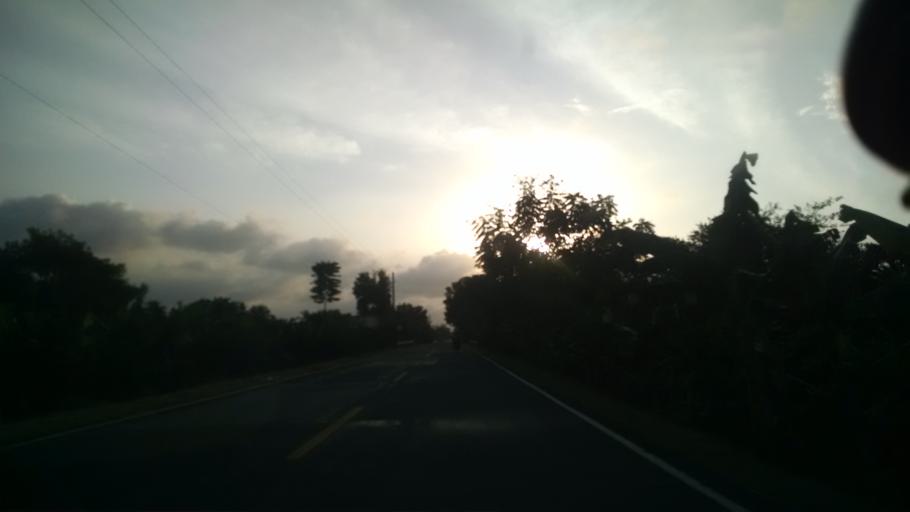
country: CO
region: Antioquia
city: San Juan de Uraba
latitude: 8.7293
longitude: -76.5839
